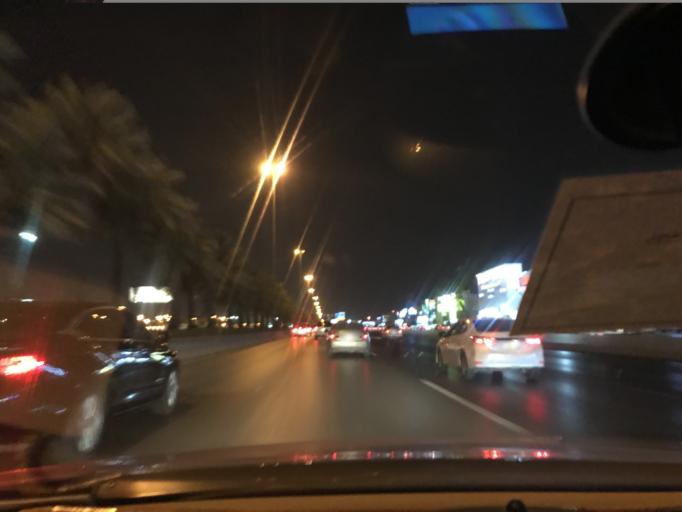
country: SA
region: Ar Riyad
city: Riyadh
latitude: 24.7476
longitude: 46.7451
